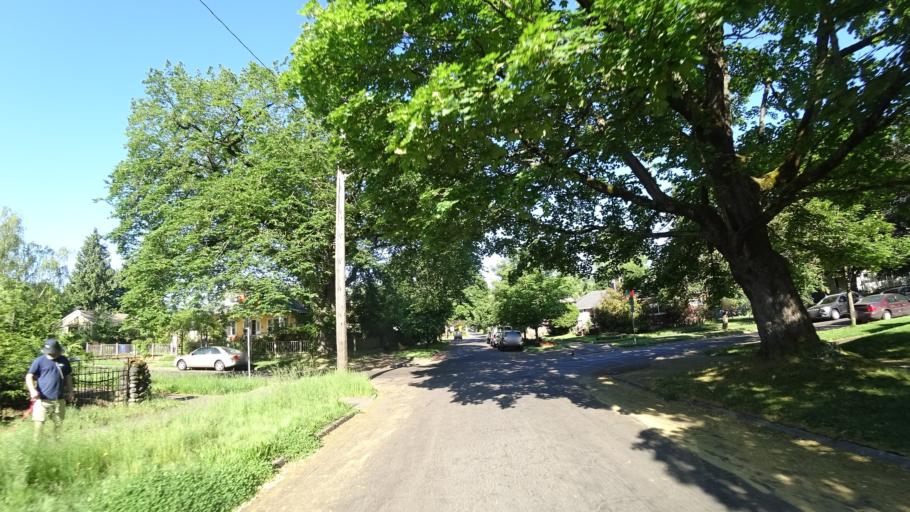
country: US
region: Oregon
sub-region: Multnomah County
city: Portland
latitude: 45.5638
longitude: -122.6657
